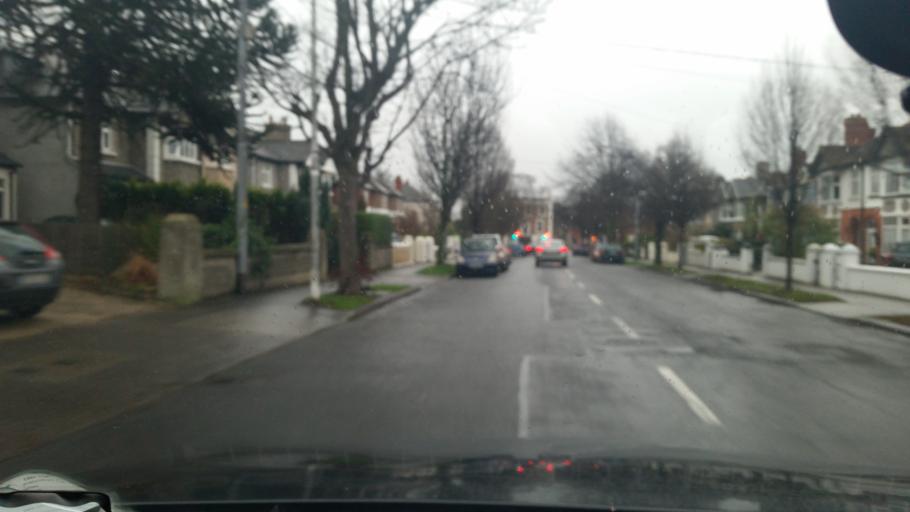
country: IE
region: Leinster
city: Marino
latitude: 53.3672
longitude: -6.2247
